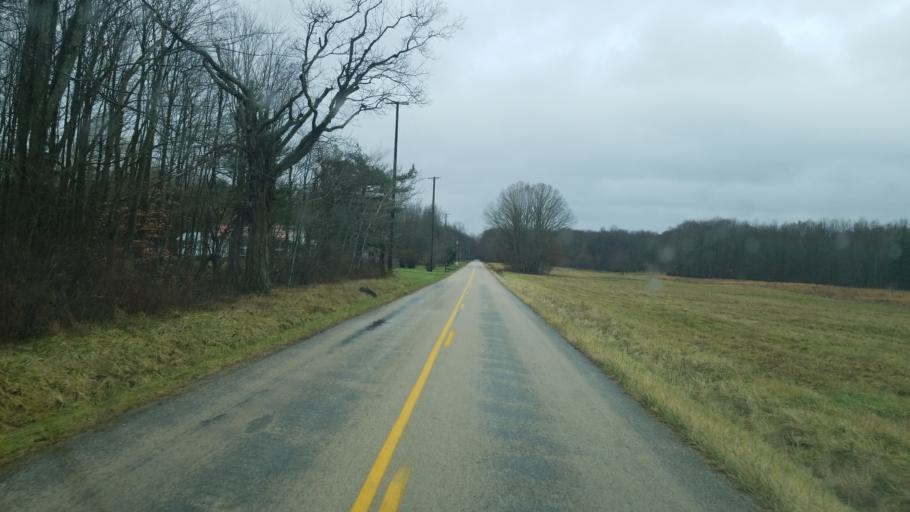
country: US
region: Ohio
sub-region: Ashtabula County
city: Roaming Shores
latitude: 41.7218
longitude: -80.8746
